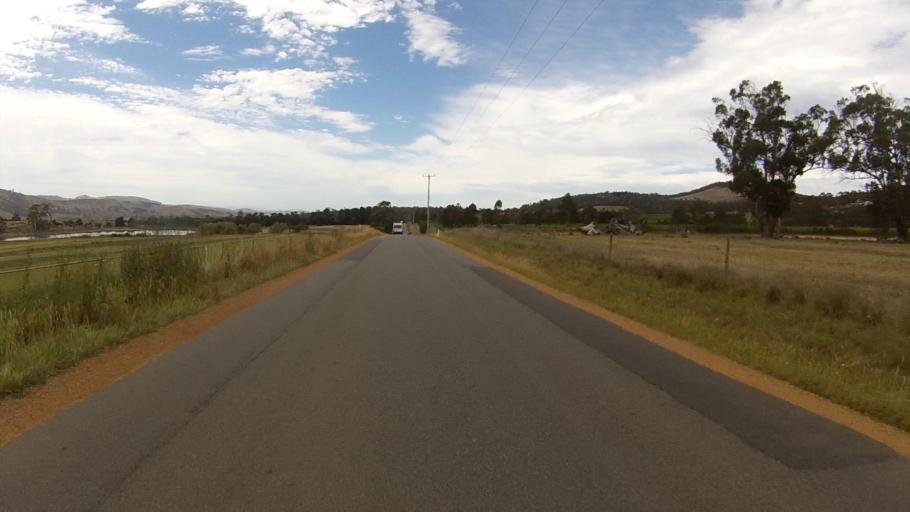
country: AU
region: Tasmania
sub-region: Clarence
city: Lindisfarne
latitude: -42.7571
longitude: 147.3830
